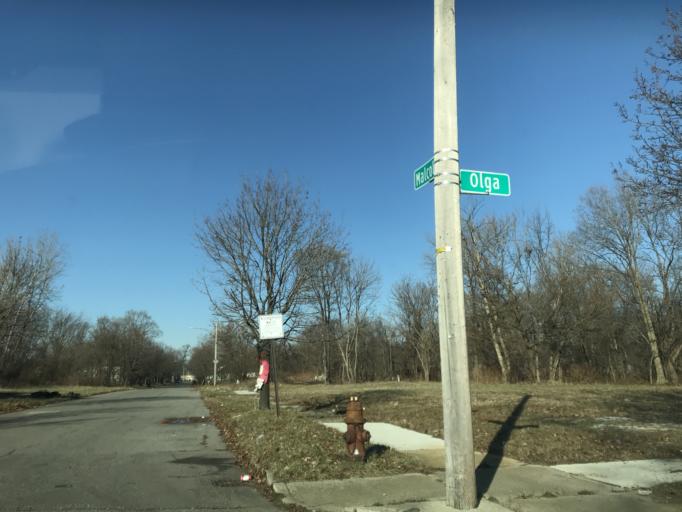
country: US
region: Michigan
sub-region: Wayne County
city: Grosse Pointe Park
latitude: 42.3945
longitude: -82.9840
